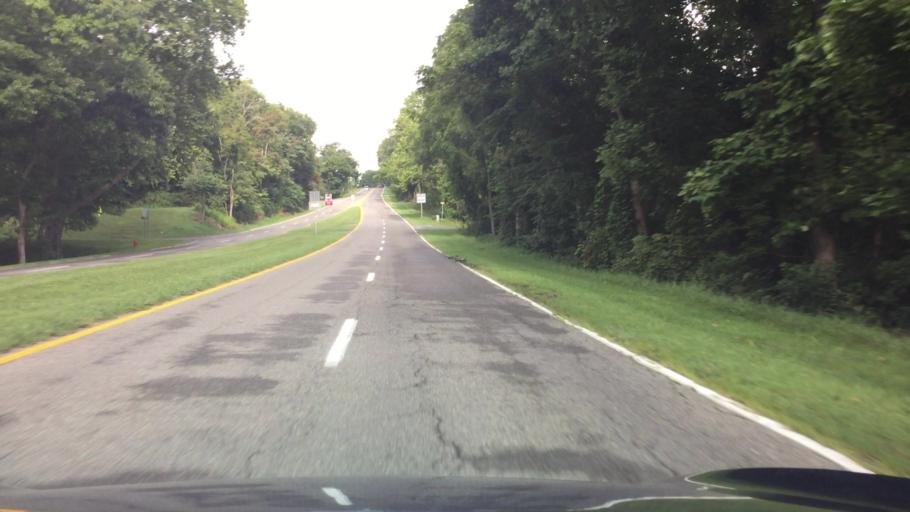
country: US
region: Virginia
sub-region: Pulaski County
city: Pulaski
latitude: 36.9496
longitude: -80.9012
